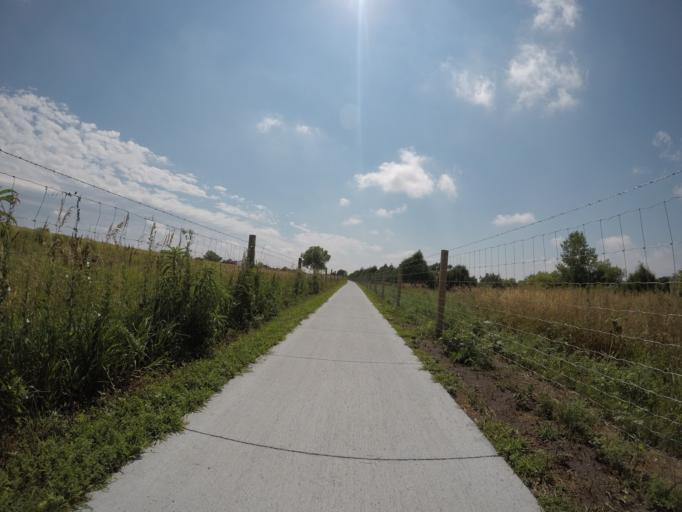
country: US
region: Nebraska
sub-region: Buffalo County
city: Kearney
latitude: 40.6784
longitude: -98.9965
